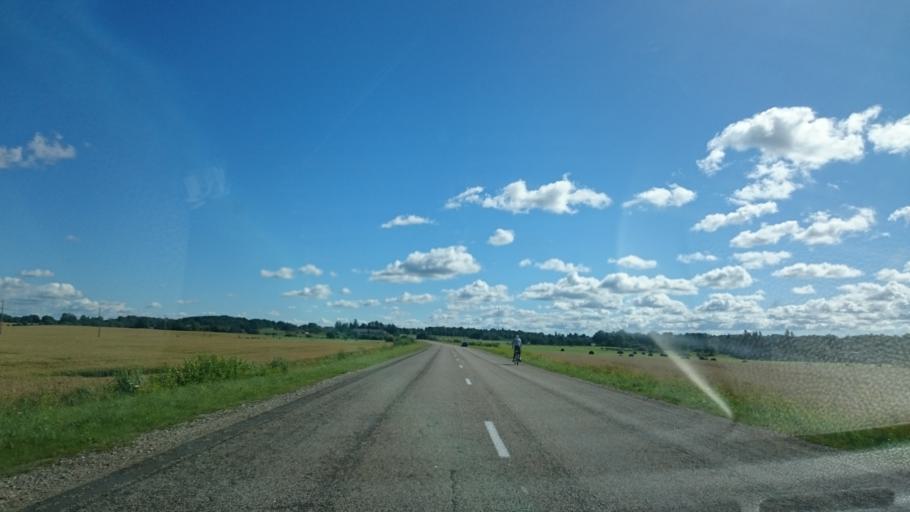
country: LV
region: Aizpute
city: Aizpute
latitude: 56.7521
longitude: 21.6138
